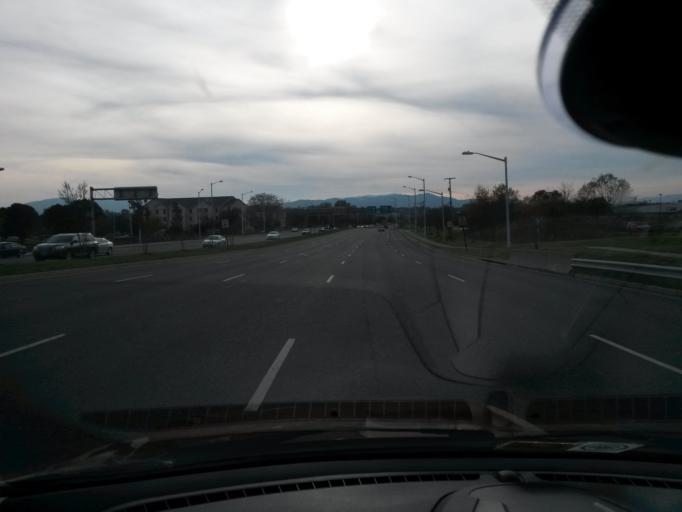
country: US
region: Virginia
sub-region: Roanoke County
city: Hollins
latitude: 37.3124
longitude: -79.9678
